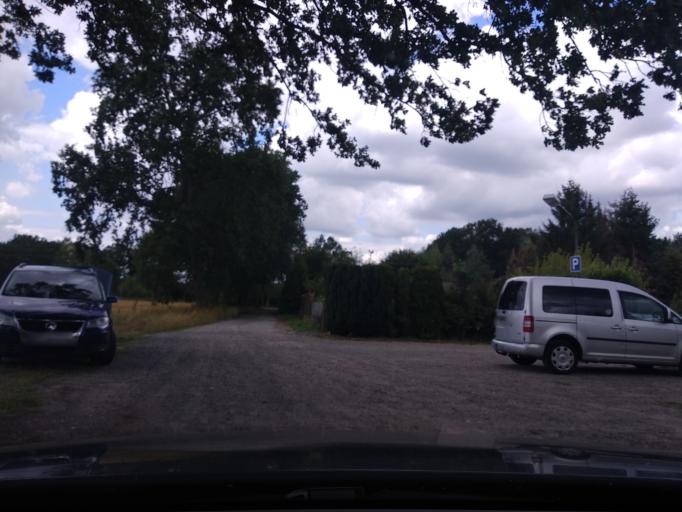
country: DE
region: Lower Saxony
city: Gifhorn
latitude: 52.5165
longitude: 10.5531
